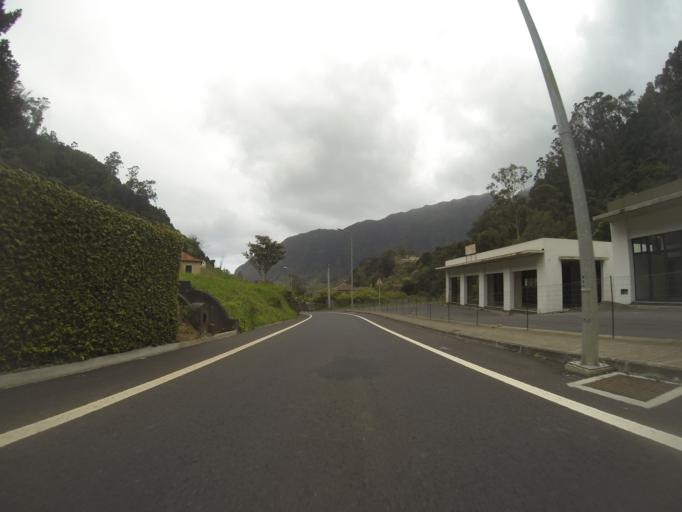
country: PT
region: Madeira
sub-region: Sao Vicente
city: Sao Vicente
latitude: 32.7842
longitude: -17.0326
